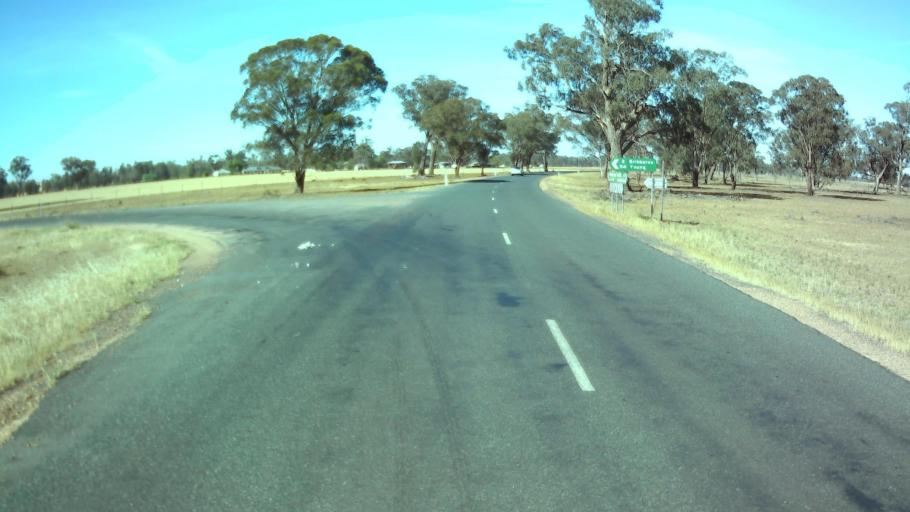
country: AU
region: New South Wales
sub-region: Weddin
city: Grenfell
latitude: -34.0965
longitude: 147.8848
